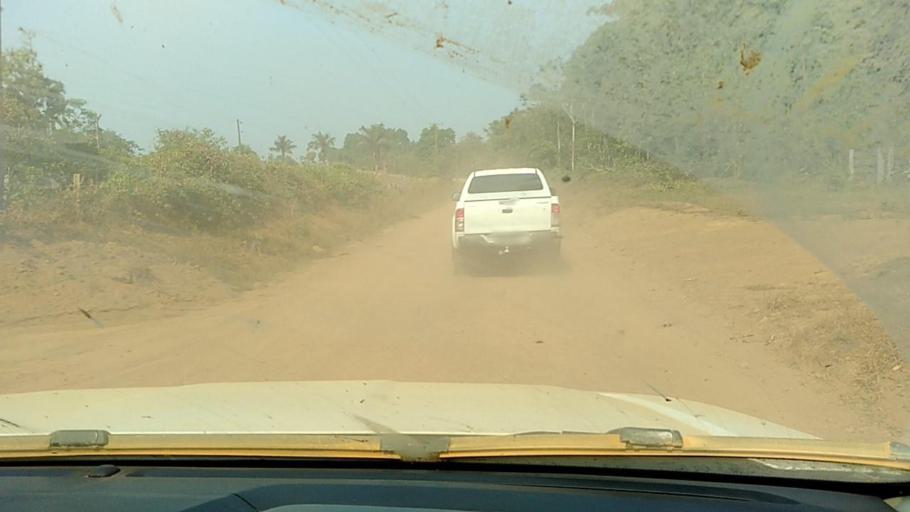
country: BR
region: Rondonia
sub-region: Porto Velho
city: Porto Velho
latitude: -8.8433
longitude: -64.1592
